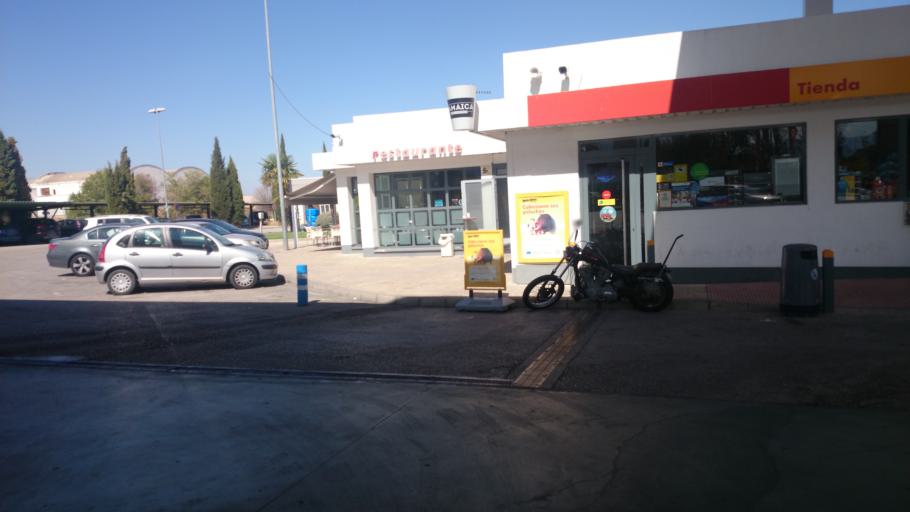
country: ES
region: Andalusia
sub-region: Provincia de Jaen
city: Jaen
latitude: 37.8173
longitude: -3.7712
